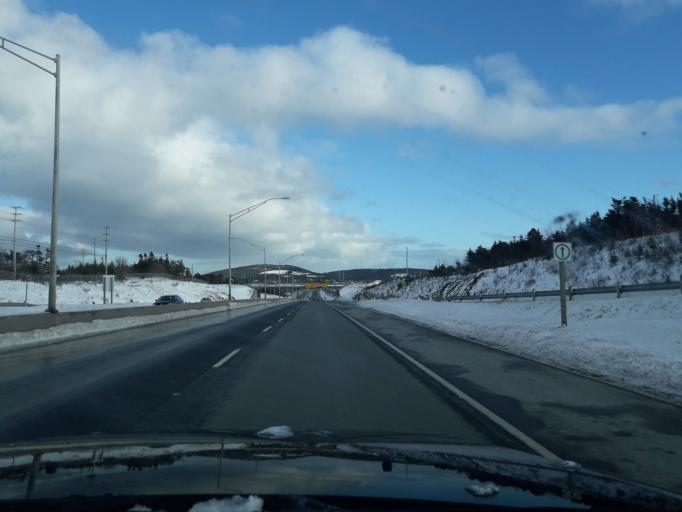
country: CA
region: Newfoundland and Labrador
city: St. John's
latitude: 47.6130
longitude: -52.7098
